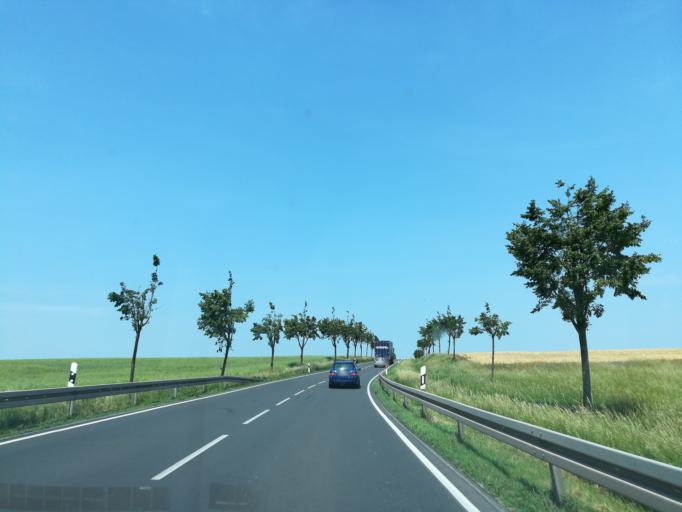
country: DE
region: Saxony-Anhalt
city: Schneidlingen
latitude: 51.8720
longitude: 11.4472
